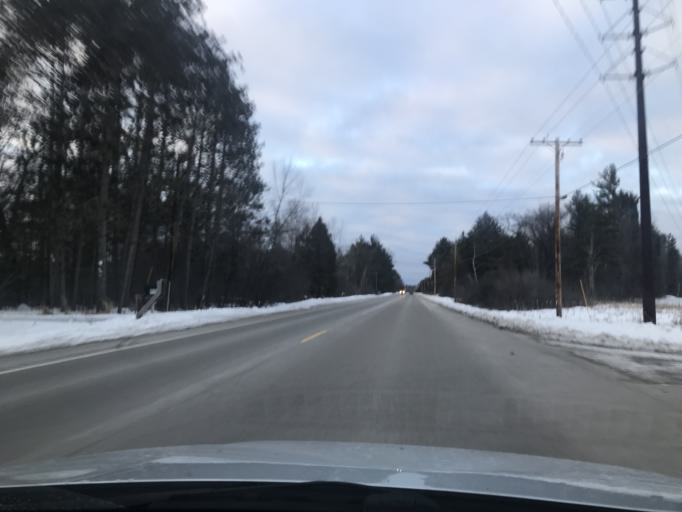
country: US
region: Wisconsin
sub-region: Marinette County
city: Marinette
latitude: 45.1283
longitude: -87.6861
